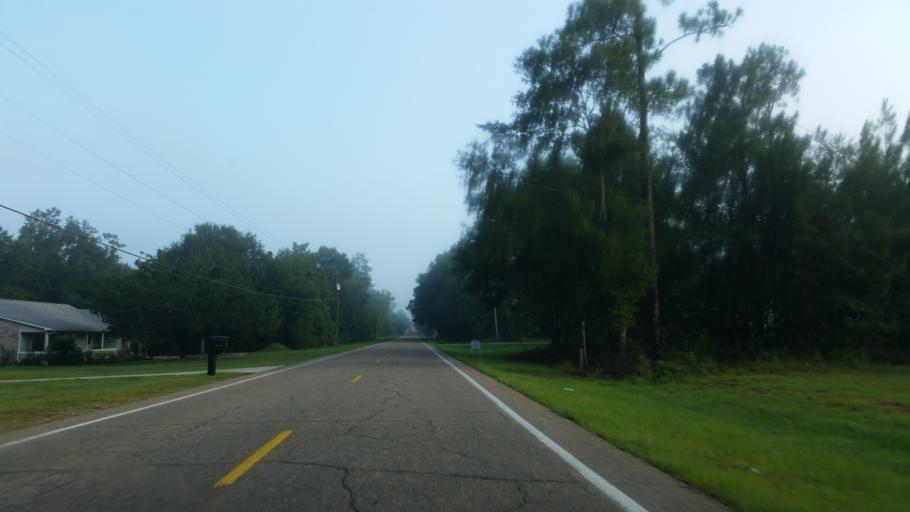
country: US
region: Florida
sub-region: Escambia County
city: Molino
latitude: 30.7345
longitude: -87.3462
